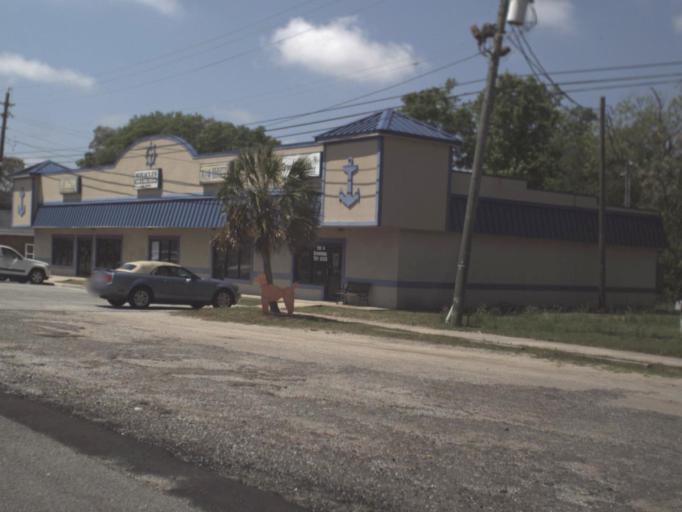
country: US
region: Florida
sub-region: Escambia County
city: Warrington
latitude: 30.3908
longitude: -87.2785
